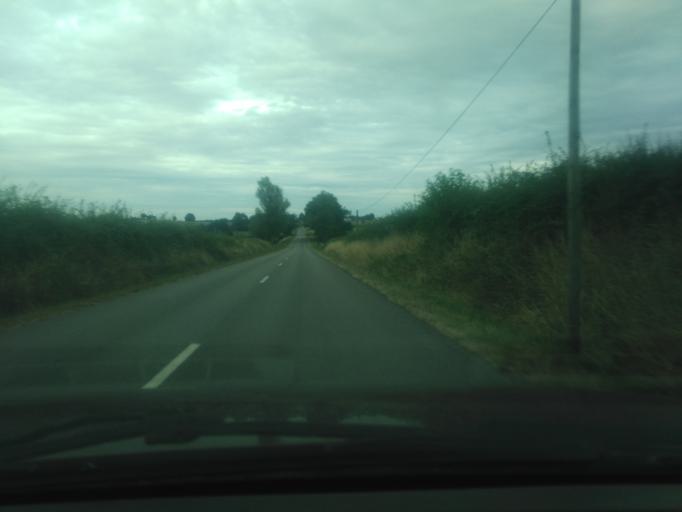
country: FR
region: Bourgogne
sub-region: Departement de la Nievre
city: Dornes
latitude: 46.7748
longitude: 3.3721
